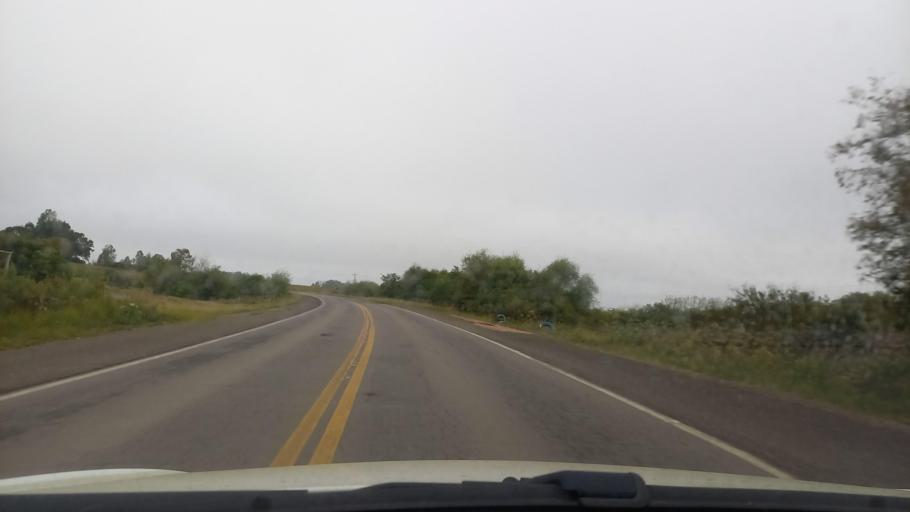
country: BR
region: Rio Grande do Sul
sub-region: Rosario Do Sul
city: Rosario do Sul
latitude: -30.1252
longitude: -54.6524
